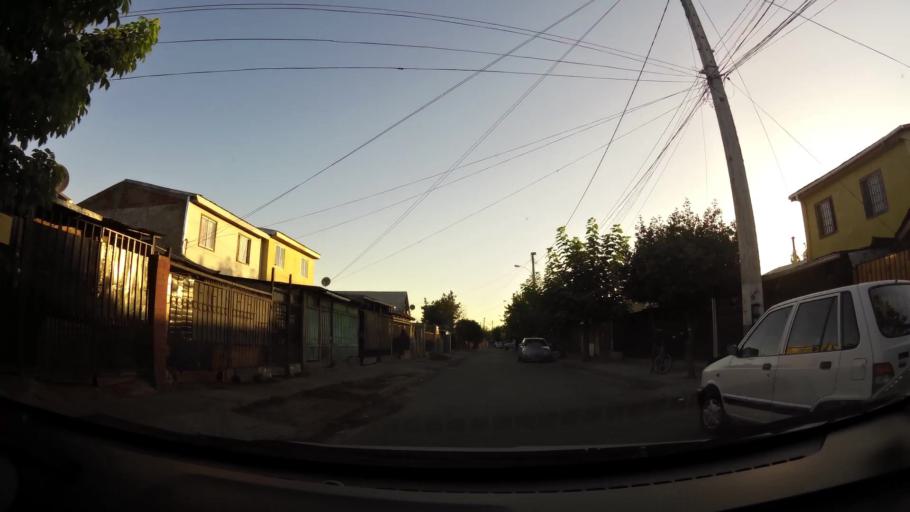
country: CL
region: Maule
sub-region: Provincia de Talca
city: Talca
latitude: -35.4448
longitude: -71.6383
